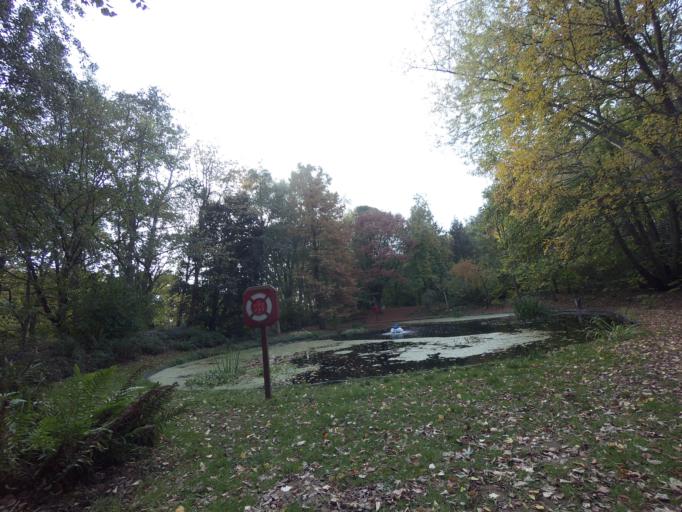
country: BE
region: Flanders
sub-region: Provincie Antwerpen
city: Brasschaat
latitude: 51.2627
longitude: 4.4583
